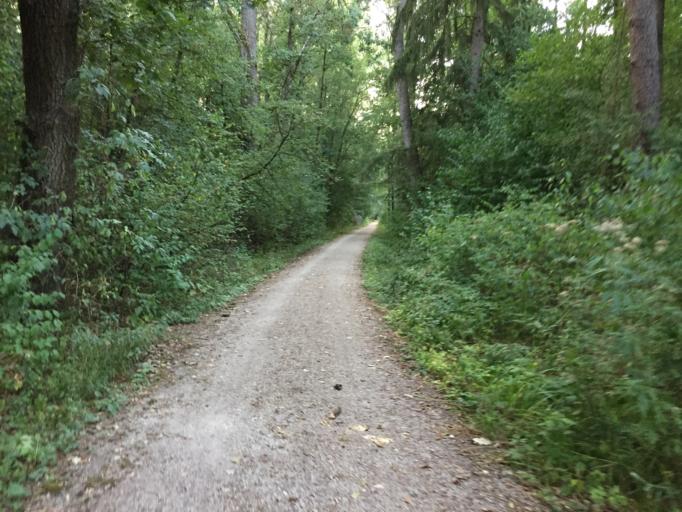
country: DE
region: Bavaria
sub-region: Regierungsbezirk Mittelfranken
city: Erlangen
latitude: 49.5662
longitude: 11.0161
